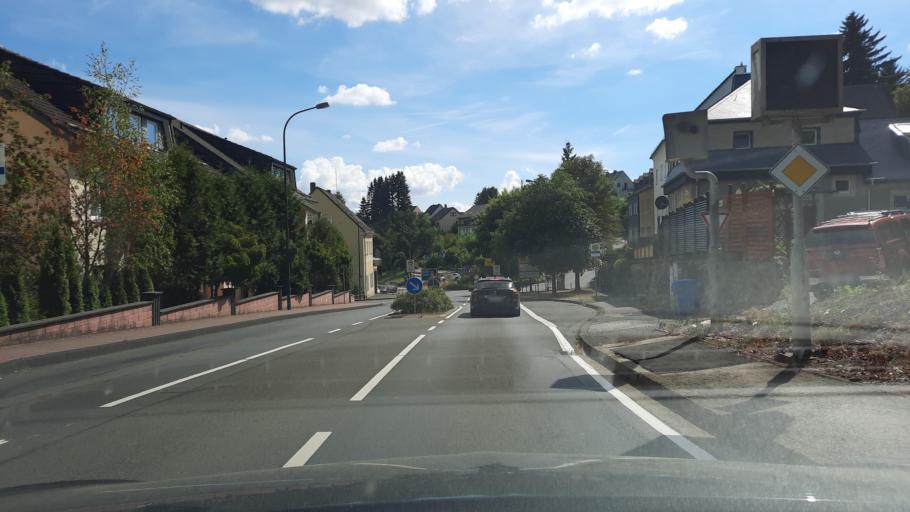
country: DE
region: Rheinland-Pfalz
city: Prum
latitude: 50.2104
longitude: 6.4152
